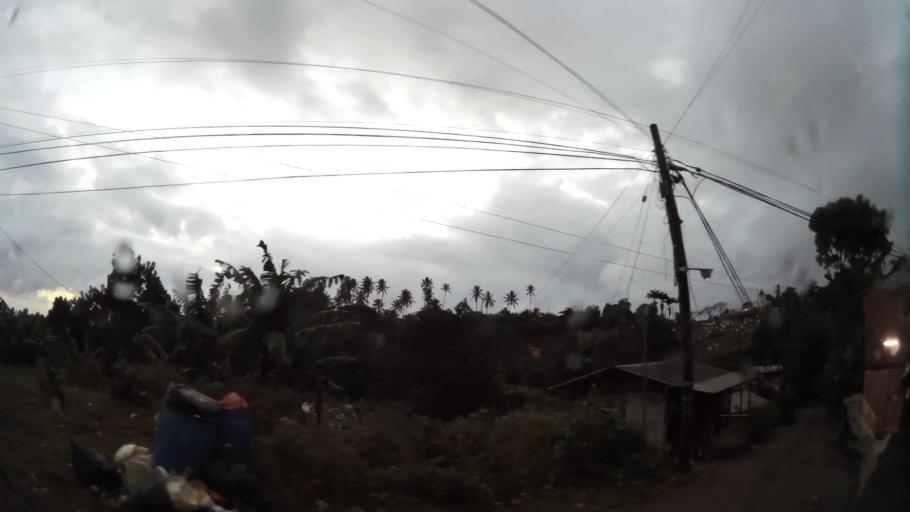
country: DM
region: Saint Andrew
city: Wesley
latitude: 15.5672
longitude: -61.3111
